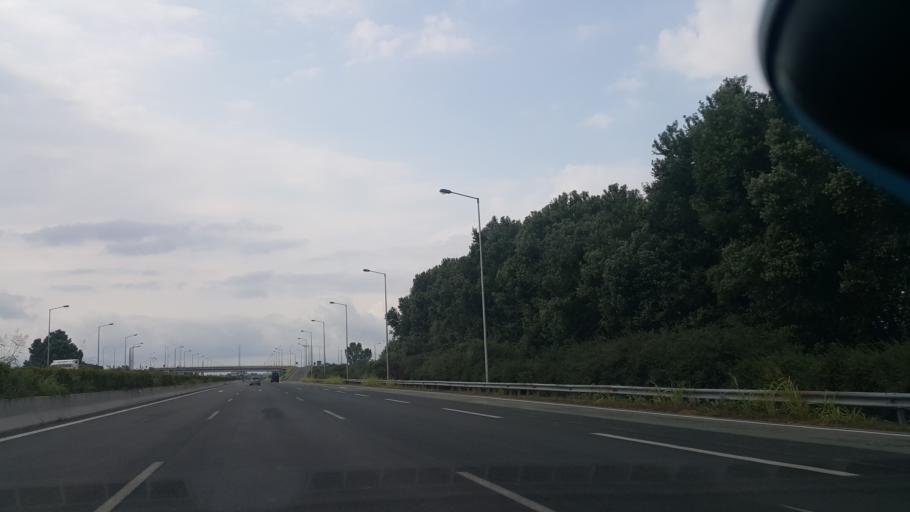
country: GR
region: Central Macedonia
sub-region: Nomos Pierias
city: Nea Efesos
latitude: 40.1977
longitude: 22.5479
